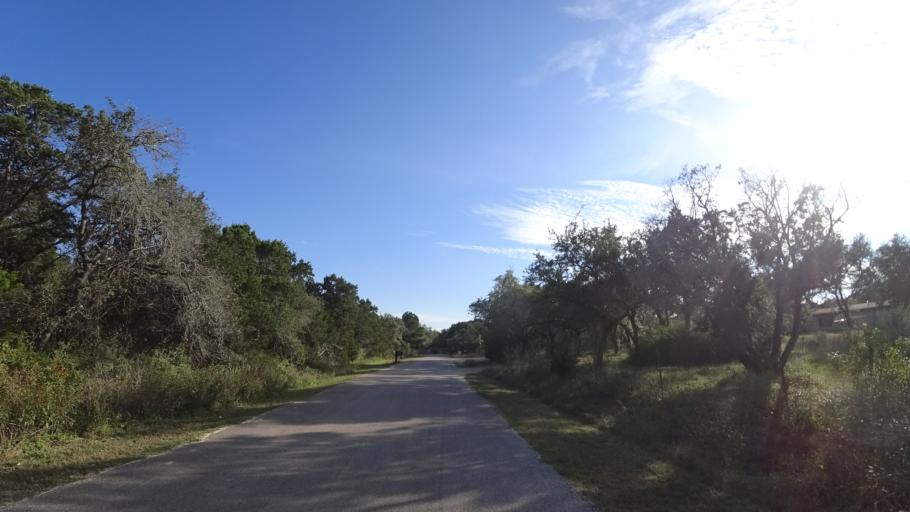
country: US
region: Texas
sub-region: Travis County
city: Bee Cave
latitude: 30.2408
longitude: -97.9354
